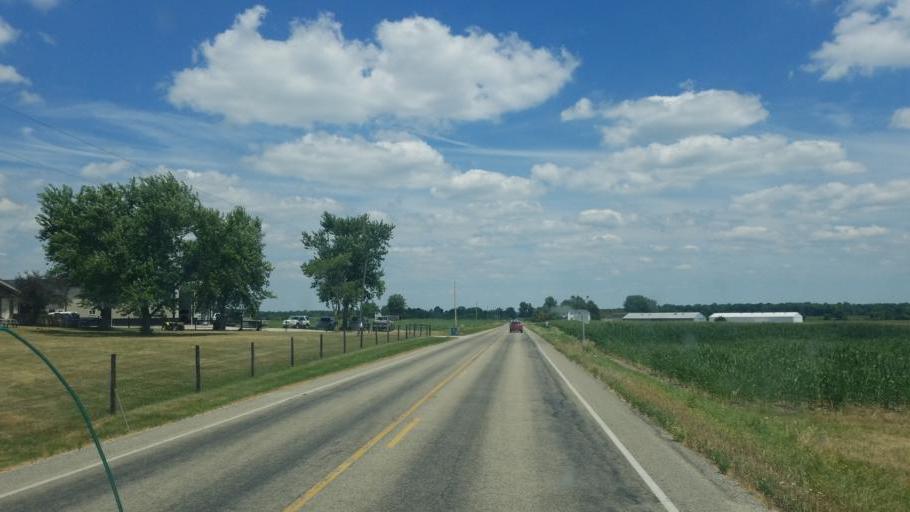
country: US
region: Ohio
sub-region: Defiance County
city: Hicksville
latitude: 41.2637
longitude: -84.8182
